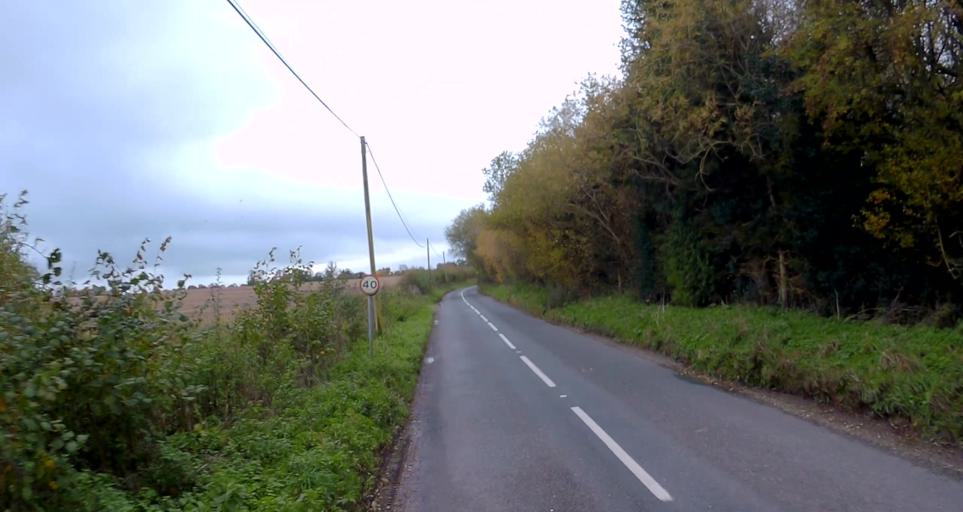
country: GB
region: England
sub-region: Hampshire
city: Four Marks
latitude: 51.1542
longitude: -1.1608
